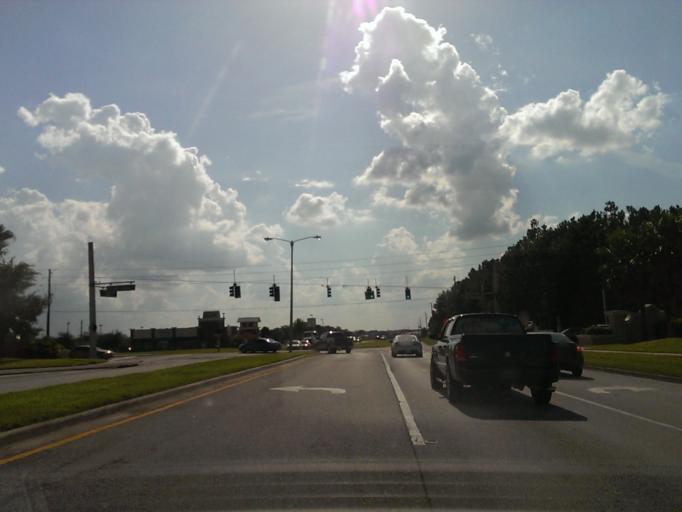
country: US
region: Florida
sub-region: Orange County
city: Oakland
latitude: 28.5180
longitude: -81.6195
